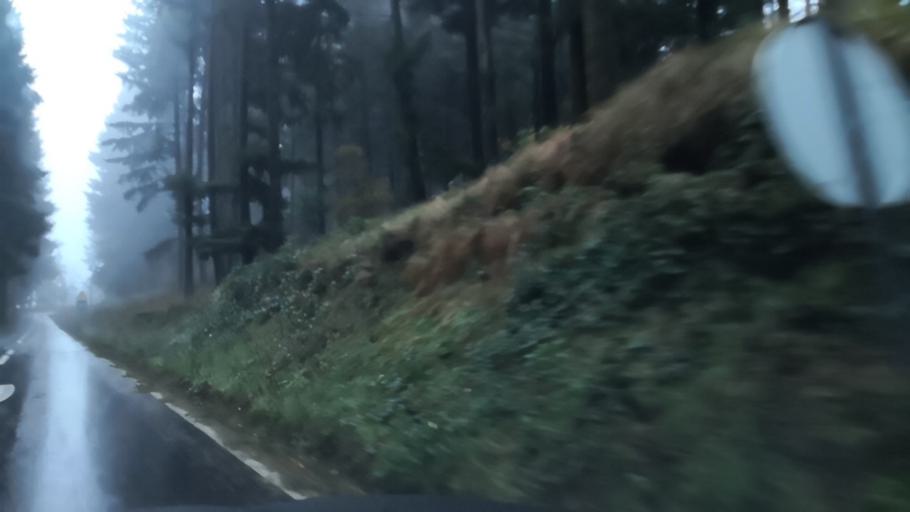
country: PT
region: Vila Real
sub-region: Vila Pouca de Aguiar
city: Vila Pouca de Aguiar
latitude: 41.5035
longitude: -7.6275
